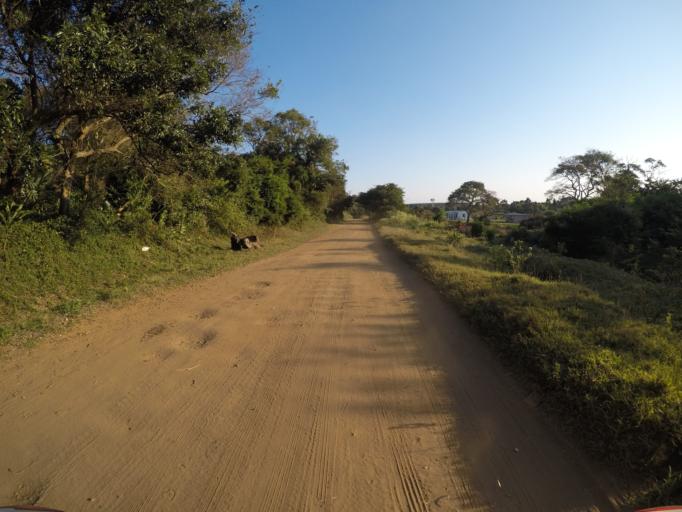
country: ZA
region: KwaZulu-Natal
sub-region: uThungulu District Municipality
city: KwaMbonambi
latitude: -28.7031
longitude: 32.1897
